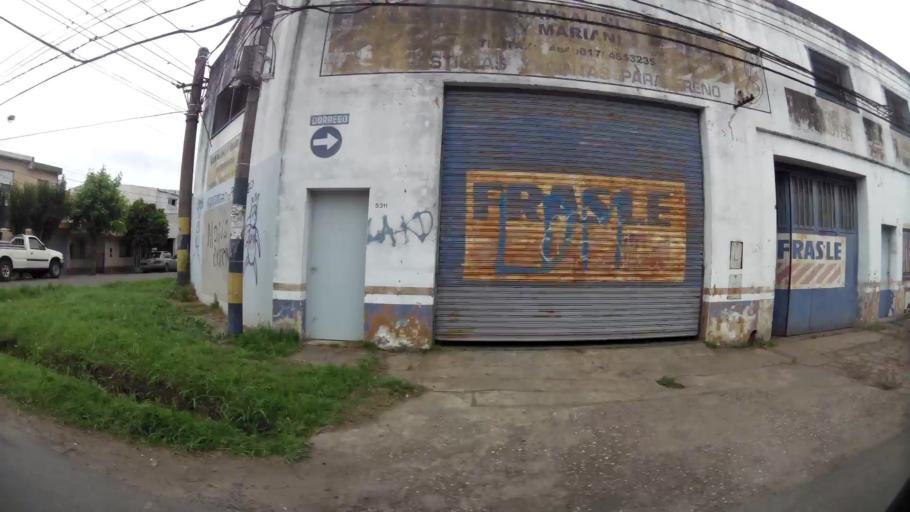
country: AR
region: Santa Fe
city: Gobernador Galvez
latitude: -32.9994
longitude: -60.6607
